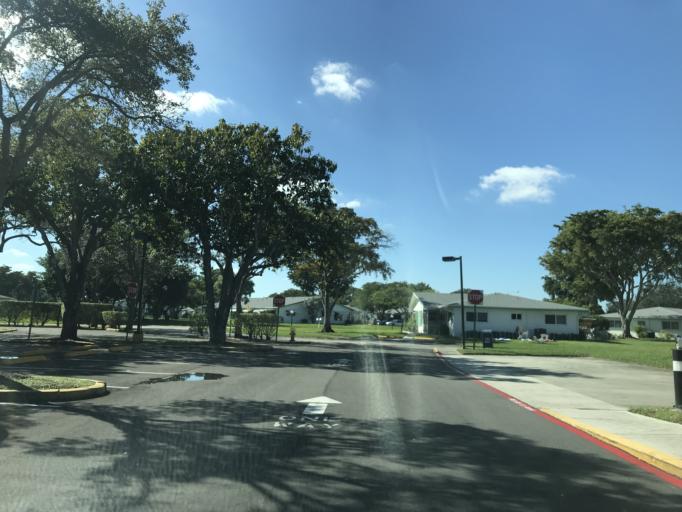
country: US
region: Florida
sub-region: Broward County
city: Plantation
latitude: 26.1391
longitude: -80.2621
